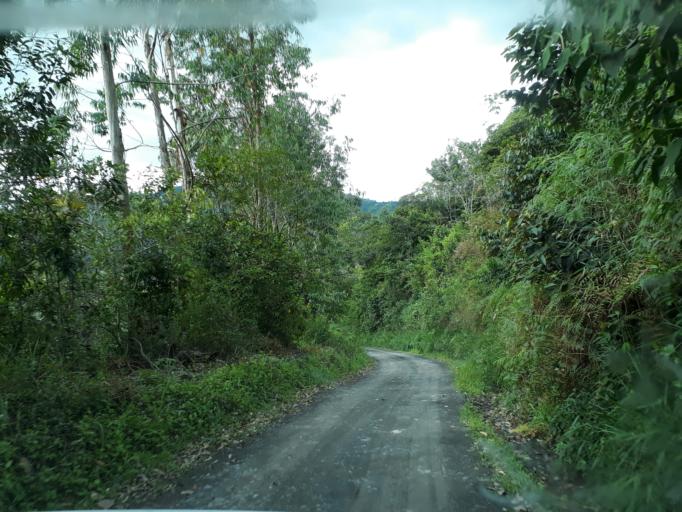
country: CO
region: Cundinamarca
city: Pacho
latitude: 5.1860
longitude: -74.2520
